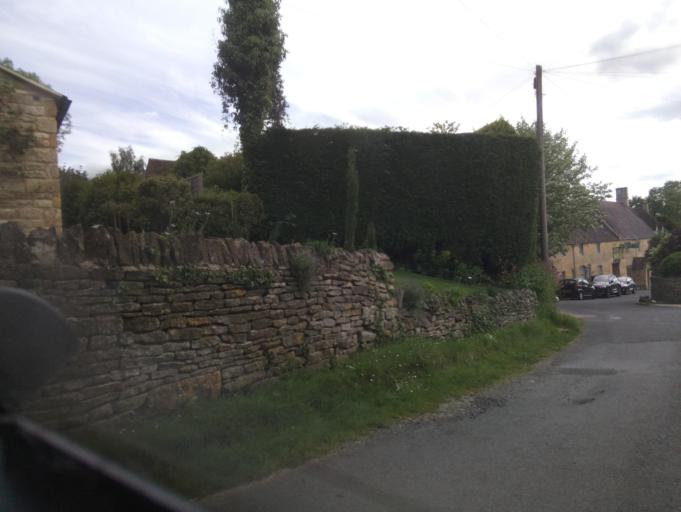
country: GB
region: England
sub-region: Gloucestershire
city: Chipping Campden
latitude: 52.0389
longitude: -1.7310
